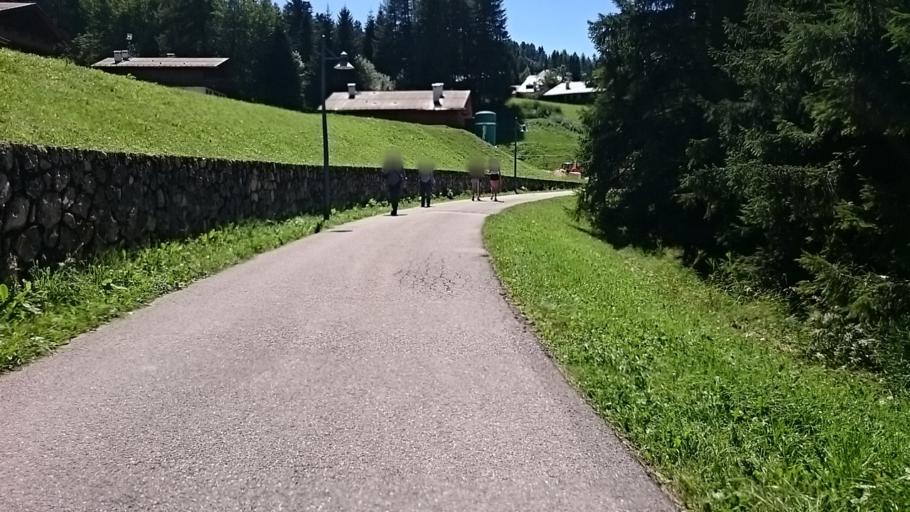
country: IT
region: Veneto
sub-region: Provincia di Belluno
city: Cortina d'Ampezzo
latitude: 46.5350
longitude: 12.1431
